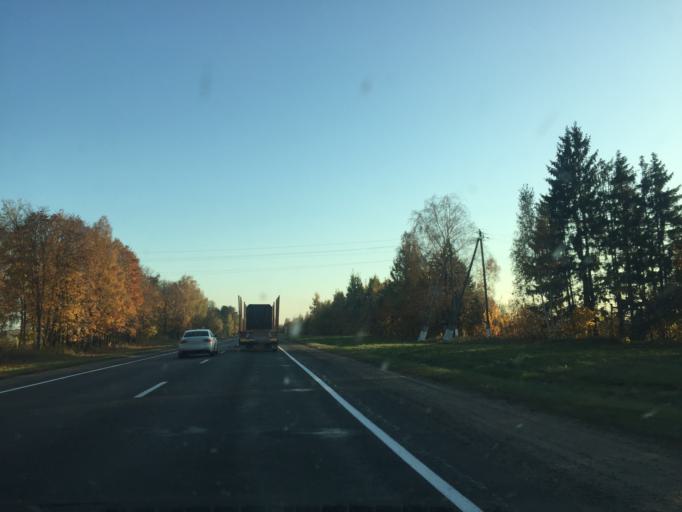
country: BY
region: Mogilev
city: Poselok Voskhod
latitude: 53.7491
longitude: 30.3656
